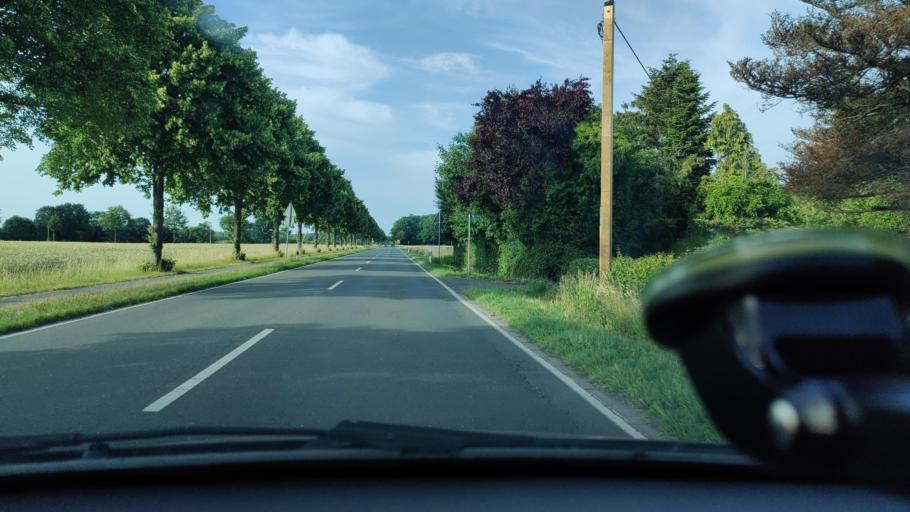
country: DE
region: North Rhine-Westphalia
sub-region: Regierungsbezirk Munster
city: Coesfeld
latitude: 51.9670
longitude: 7.1878
